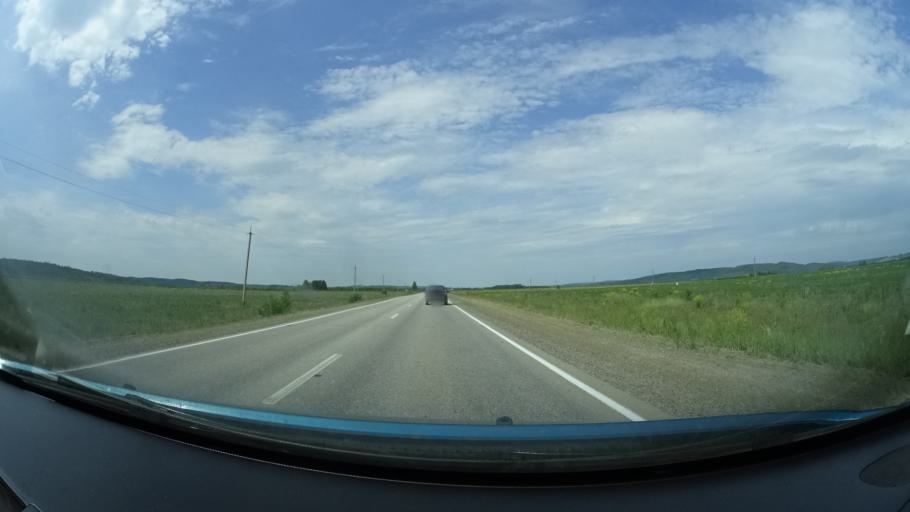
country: RU
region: Perm
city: Barda
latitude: 57.0427
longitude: 55.5462
